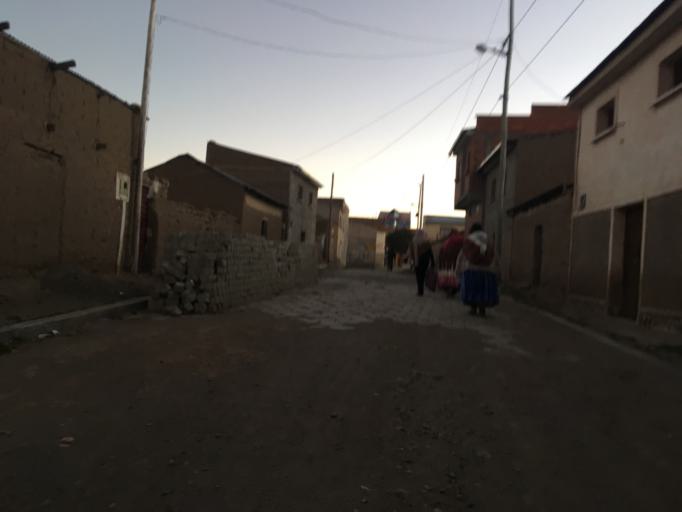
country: PE
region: Puno
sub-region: Provincia de Chucuito
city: Kelluyo
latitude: -17.0651
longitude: -69.1918
